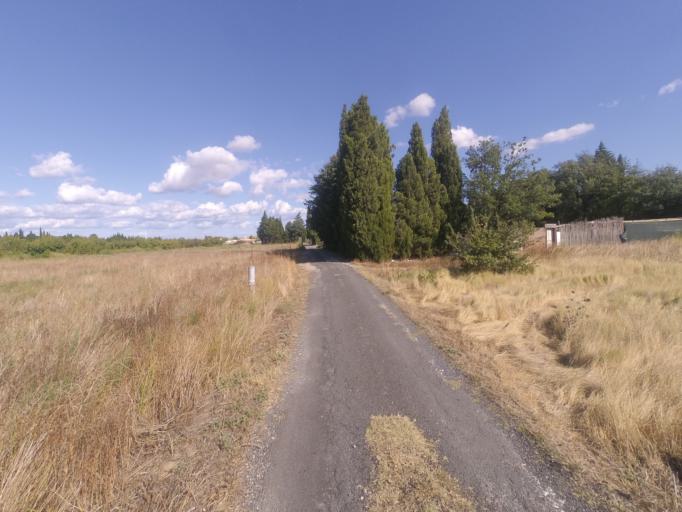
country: FR
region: Languedoc-Roussillon
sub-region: Departement des Pyrenees-Orientales
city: Corneilla-la-Riviere
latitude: 42.6956
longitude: 2.7200
